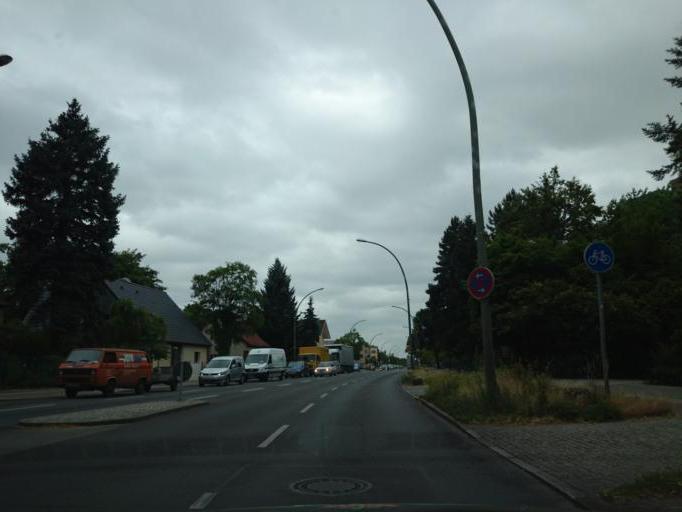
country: DE
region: Berlin
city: Marienfelde
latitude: 52.4105
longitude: 13.3603
